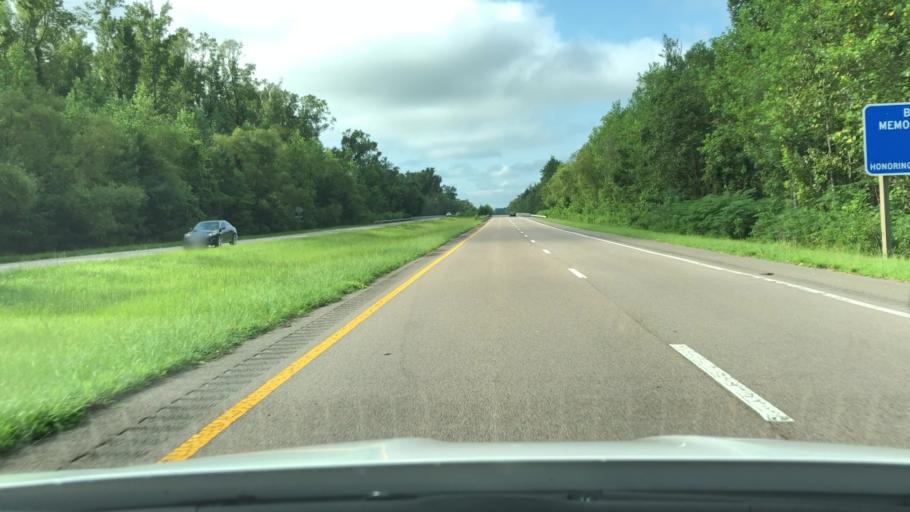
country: US
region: Virginia
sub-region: City of Portsmouth
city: Portsmouth Heights
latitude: 36.6359
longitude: -76.3631
